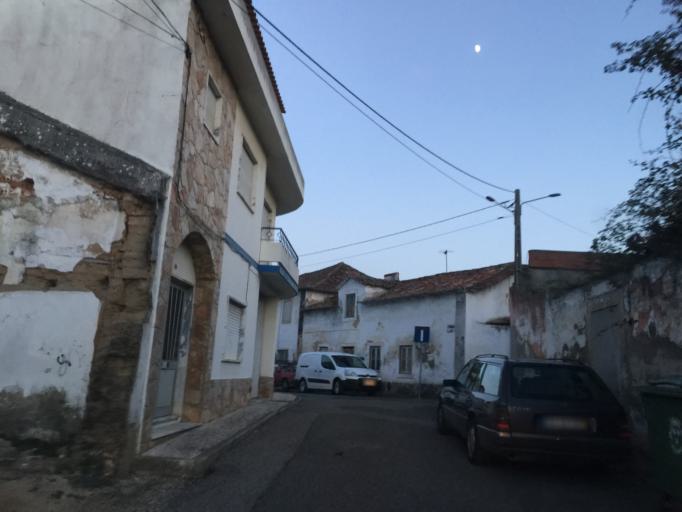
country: PT
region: Leiria
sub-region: Bombarral
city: Bombarral
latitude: 39.2670
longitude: -9.1595
